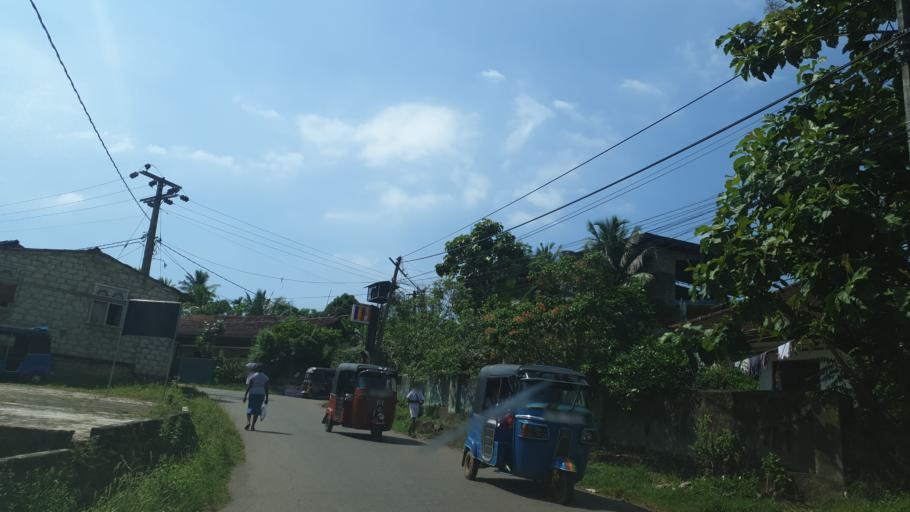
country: LK
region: Western
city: Panadura
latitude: 6.7221
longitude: 79.9578
